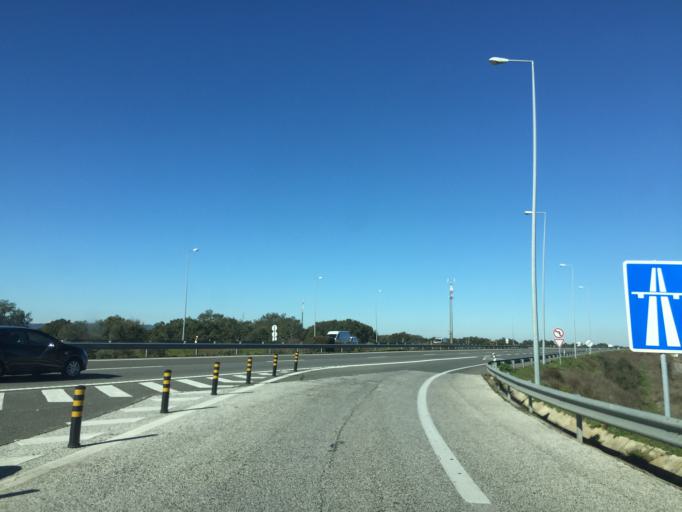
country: PT
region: Setubal
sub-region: Grandola
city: Grandola
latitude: 38.1683
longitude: -8.4910
